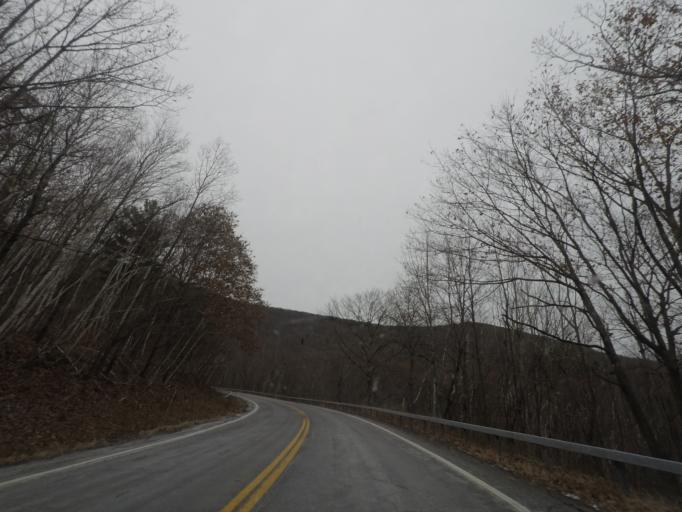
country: US
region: Massachusetts
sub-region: Berkshire County
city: Williamstown
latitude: 42.7427
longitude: -73.2864
